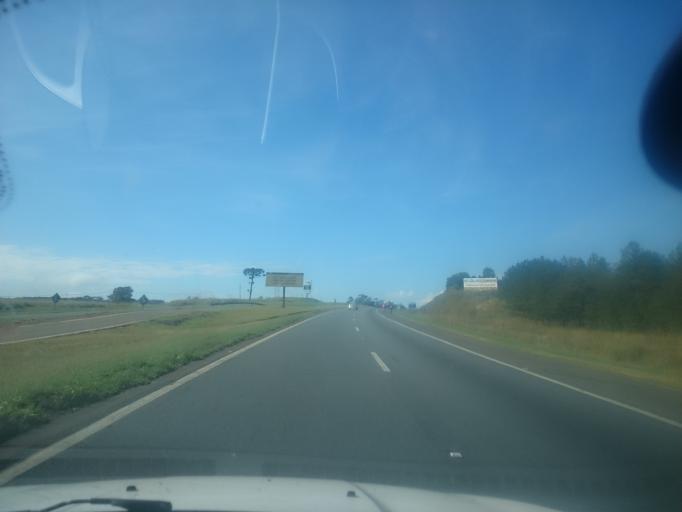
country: BR
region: Parana
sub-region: Campo Largo
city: Campo Largo
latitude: -25.4706
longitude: -49.6886
